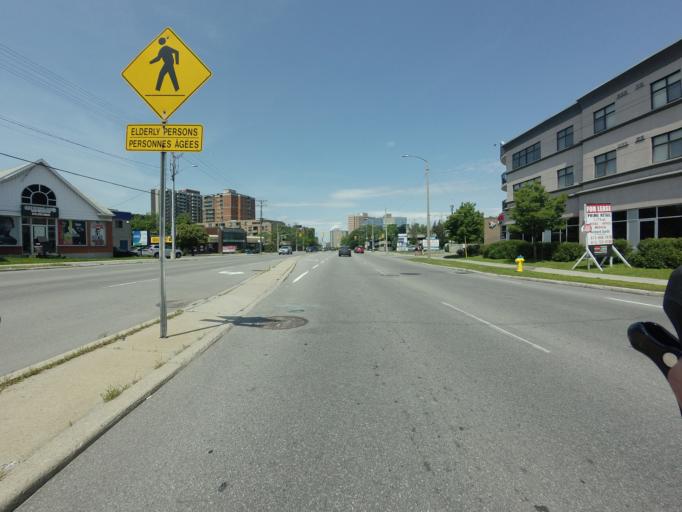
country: CA
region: Ontario
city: Ottawa
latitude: 45.3829
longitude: -75.6711
